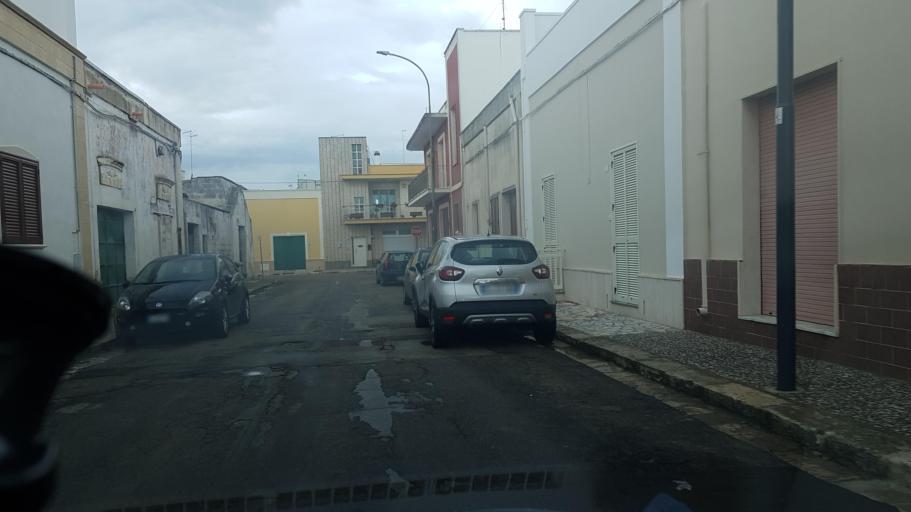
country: IT
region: Apulia
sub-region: Provincia di Lecce
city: Salice Salentino
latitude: 40.3841
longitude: 17.9680
